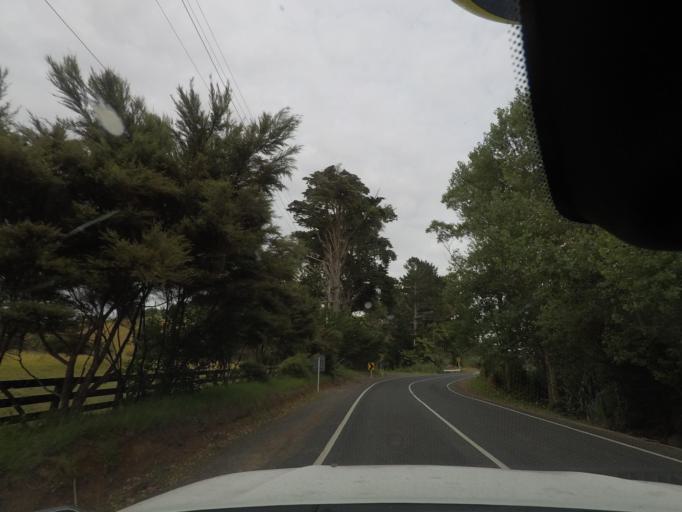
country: NZ
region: Auckland
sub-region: Auckland
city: Parakai
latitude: -36.5257
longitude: 174.2895
